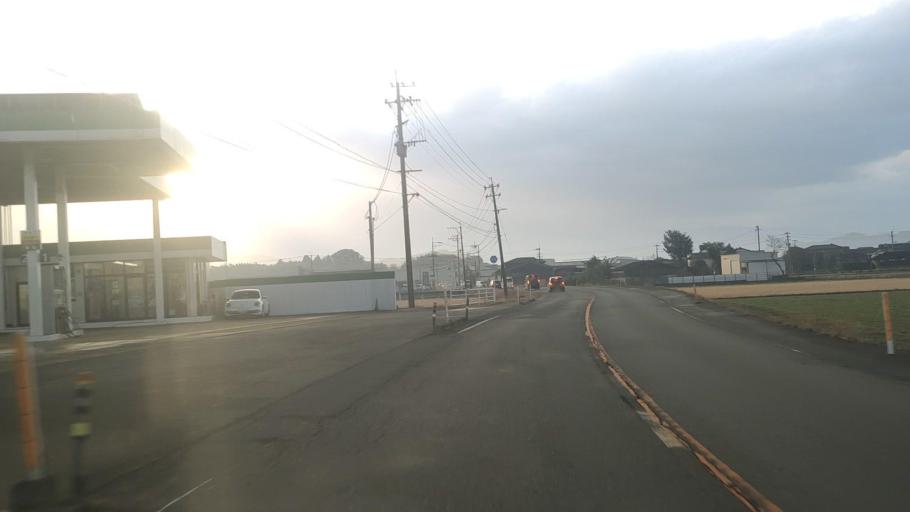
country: JP
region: Kumamoto
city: Uto
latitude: 32.7257
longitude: 130.7656
